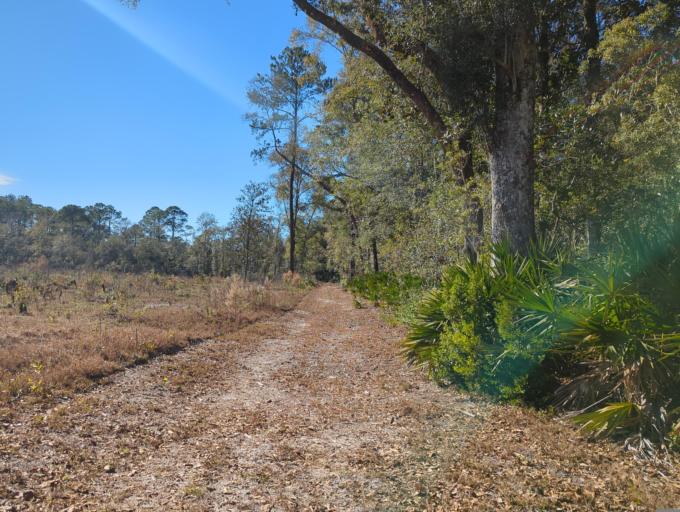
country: US
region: Florida
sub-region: Wakulla County
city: Crawfordville
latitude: 30.1878
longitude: -84.3308
